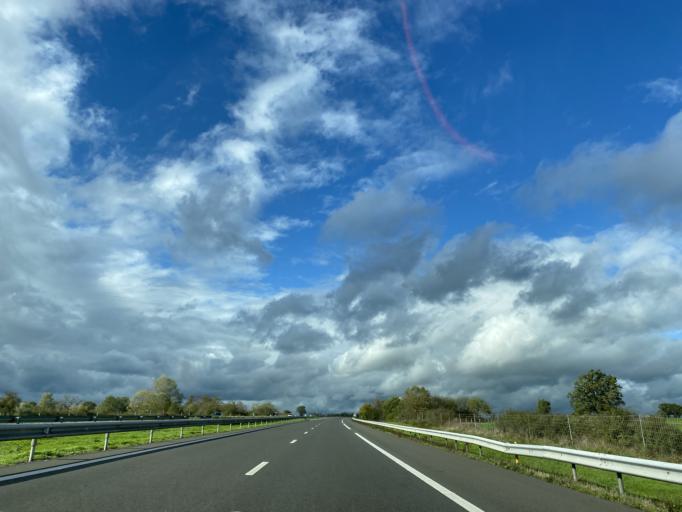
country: FR
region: Auvergne
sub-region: Departement de l'Allier
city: Bellenaves
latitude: 46.2609
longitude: 3.0697
